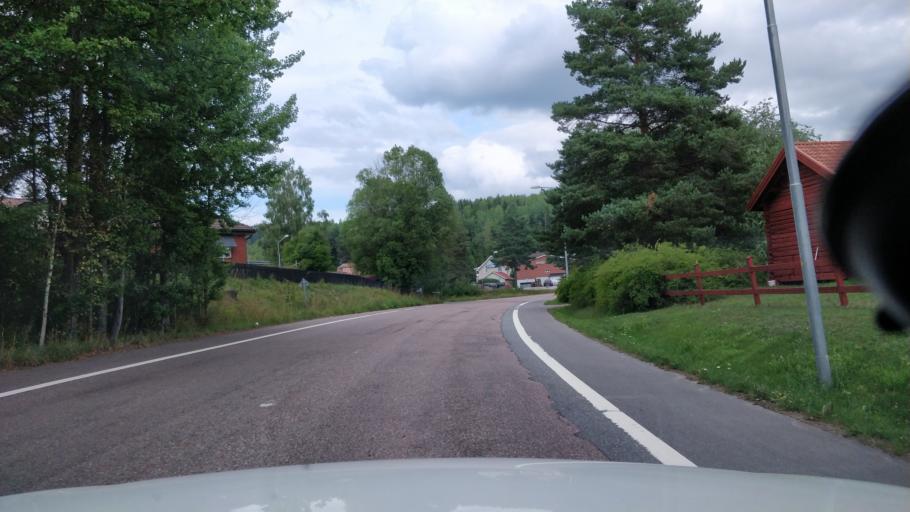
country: SE
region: Dalarna
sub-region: Faluns Kommun
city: Bjursas
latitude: 60.7380
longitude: 15.4405
